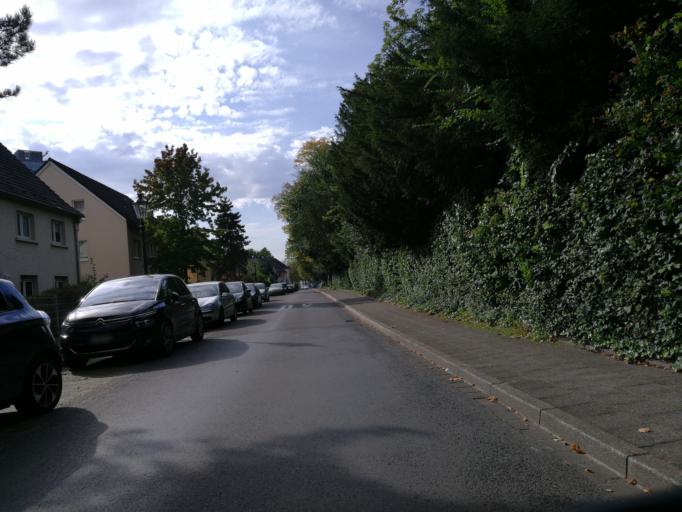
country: DE
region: North Rhine-Westphalia
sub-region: Regierungsbezirk Dusseldorf
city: Dusseldorf
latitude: 51.2549
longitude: 6.7752
